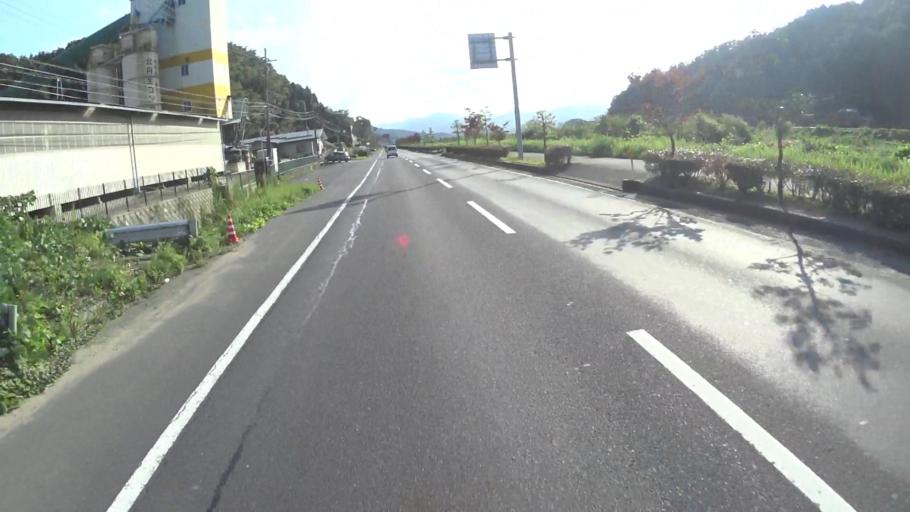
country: JP
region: Kyoto
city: Miyazu
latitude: 35.5495
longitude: 135.1375
